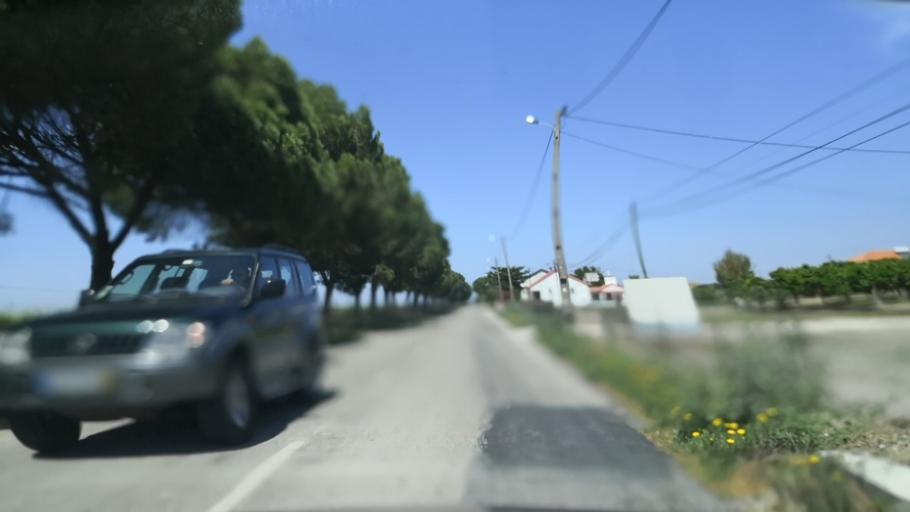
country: PT
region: Santarem
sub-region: Benavente
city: Poceirao
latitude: 38.6759
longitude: -8.7341
